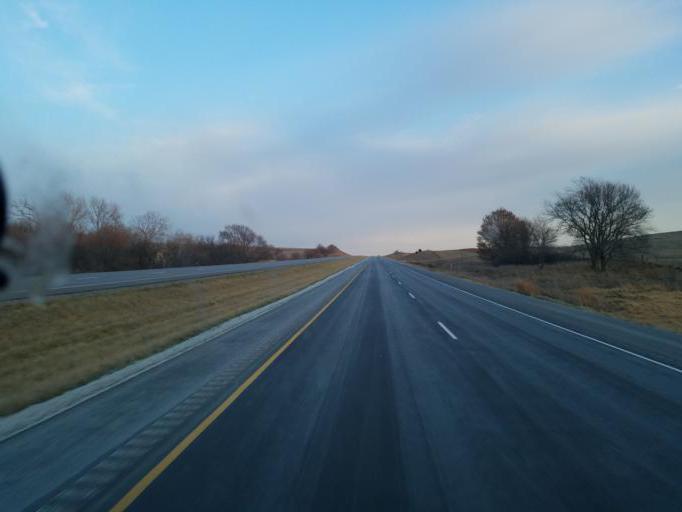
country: US
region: Iowa
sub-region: Harrison County
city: Logan
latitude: 41.4988
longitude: -95.6528
